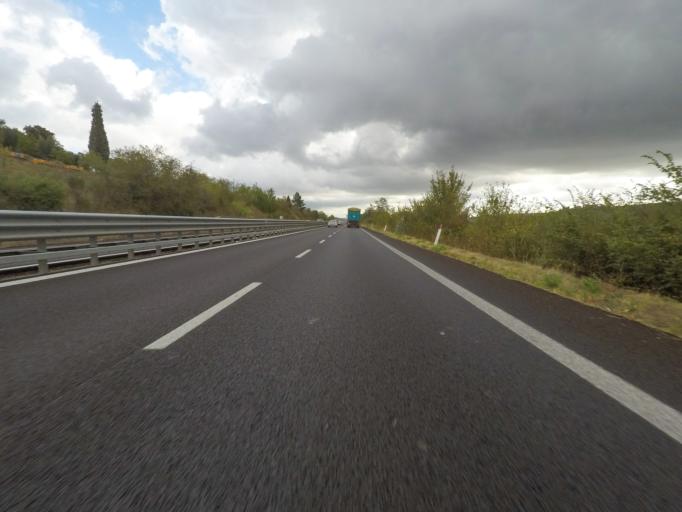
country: IT
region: Tuscany
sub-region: Provincia di Siena
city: Arbia
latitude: 43.3065
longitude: 11.4414
